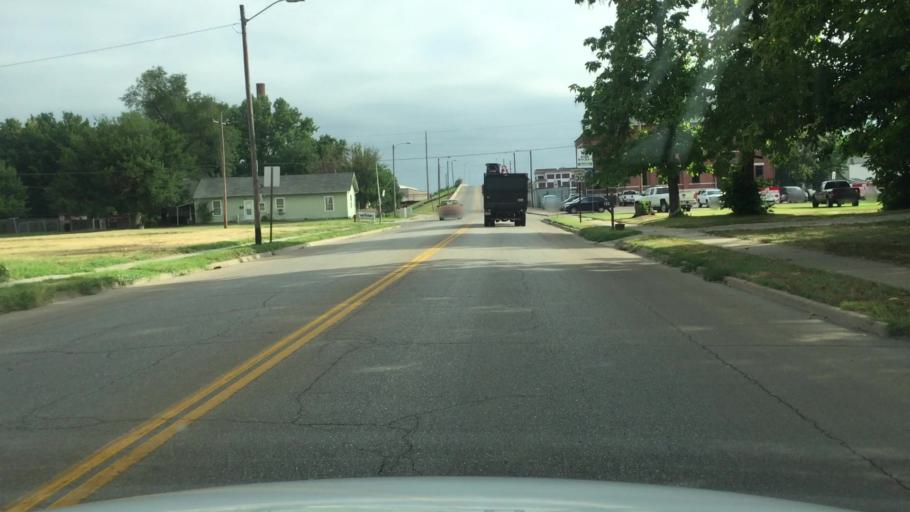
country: US
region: Kansas
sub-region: Shawnee County
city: Topeka
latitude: 39.0520
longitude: -95.6595
